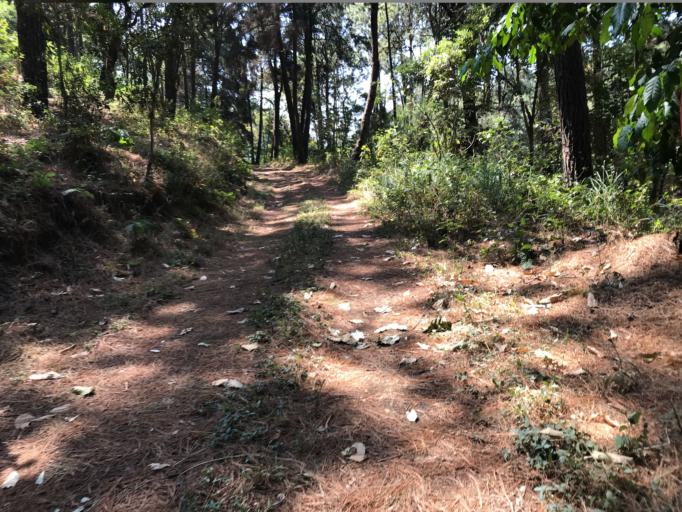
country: GT
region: Guatemala
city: Villa Canales
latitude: 14.4816
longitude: -90.5493
